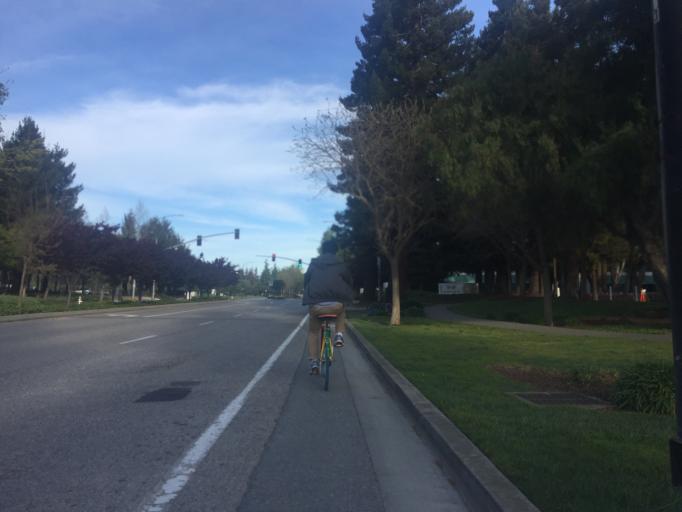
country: US
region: California
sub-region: Santa Clara County
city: Mountain View
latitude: 37.4208
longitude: -122.0840
